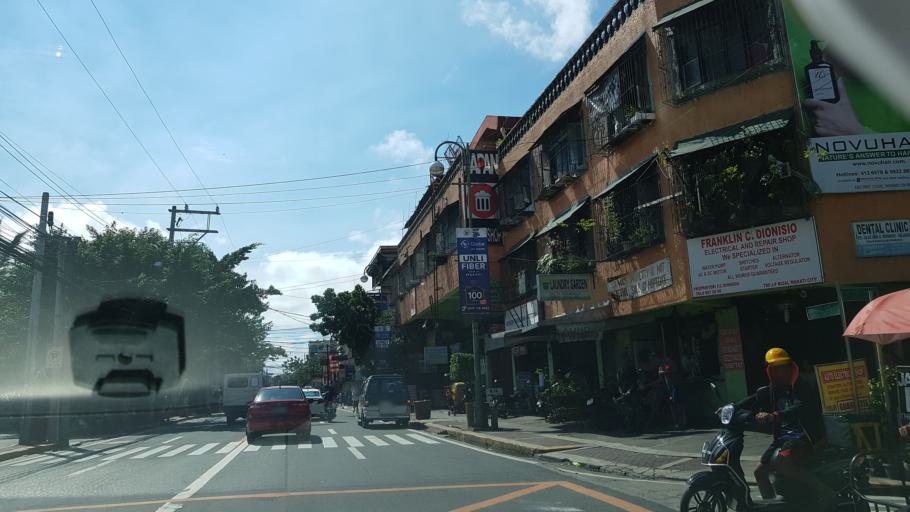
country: PH
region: Metro Manila
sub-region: Makati City
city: Makati City
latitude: 14.5701
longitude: 121.0233
